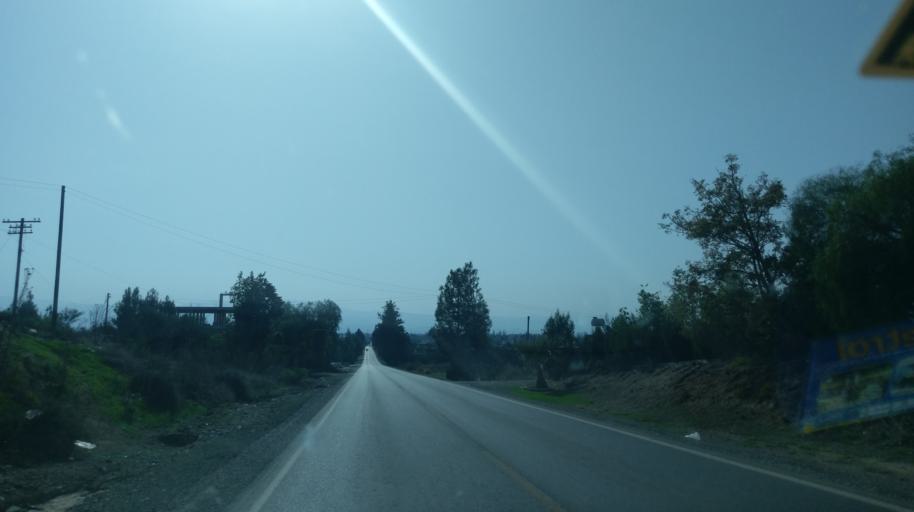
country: CY
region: Lefkosia
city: Morfou
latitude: 35.2259
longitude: 33.0116
